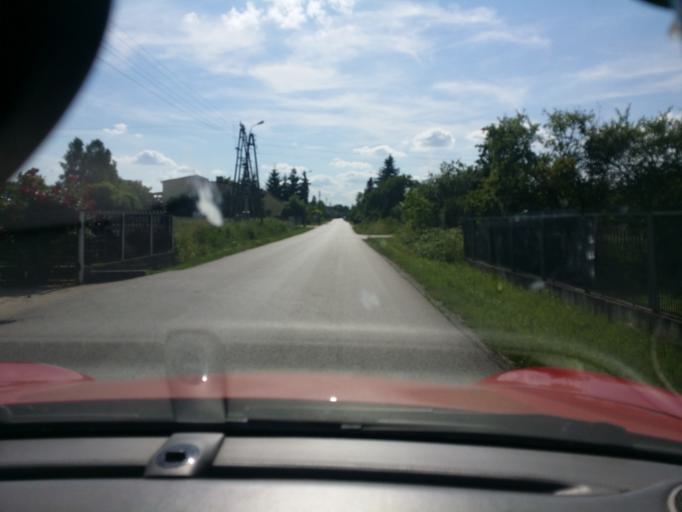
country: PL
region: Masovian Voivodeship
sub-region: Powiat radomski
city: Trablice
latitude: 51.3480
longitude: 21.1023
